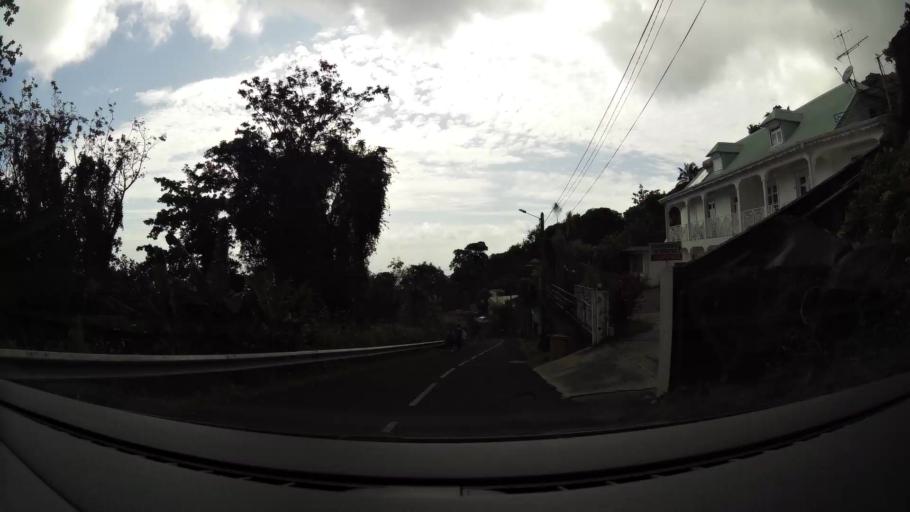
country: GP
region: Guadeloupe
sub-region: Guadeloupe
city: Trois-Rivieres
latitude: 15.9743
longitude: -61.6438
